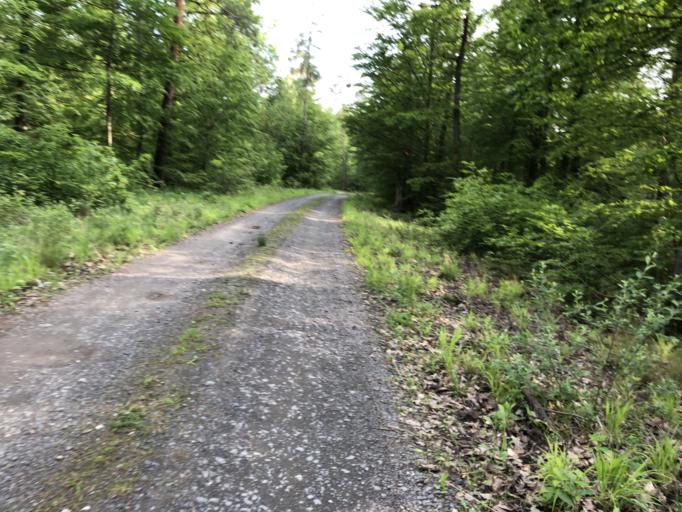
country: DE
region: Bavaria
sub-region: Upper Franconia
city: Memmelsdorf
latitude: 49.9121
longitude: 10.9562
